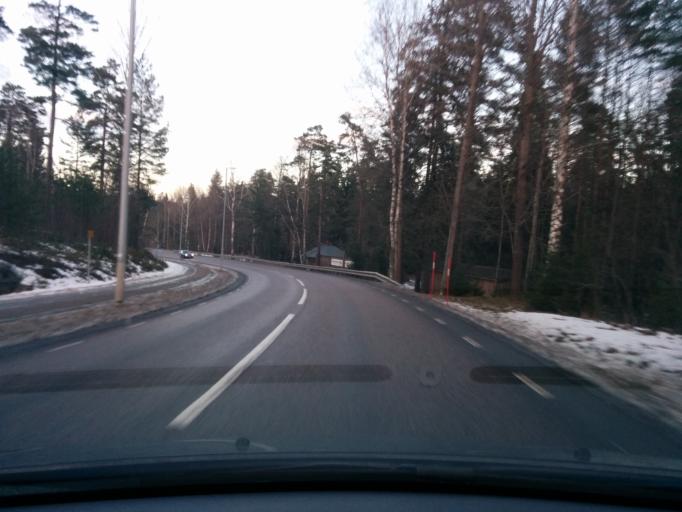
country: SE
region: Stockholm
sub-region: Nacka Kommun
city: Alta
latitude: 59.2801
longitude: 18.1823
